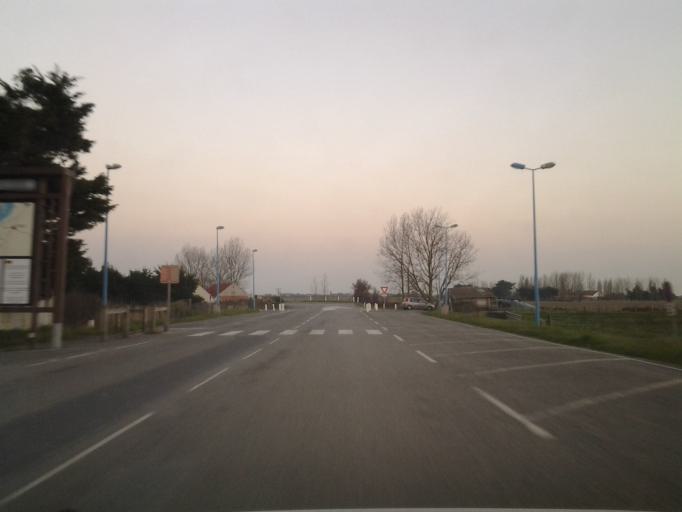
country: FR
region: Pays de la Loire
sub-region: Departement de la Vendee
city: La Barre-de-Monts
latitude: 46.9206
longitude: -2.1029
